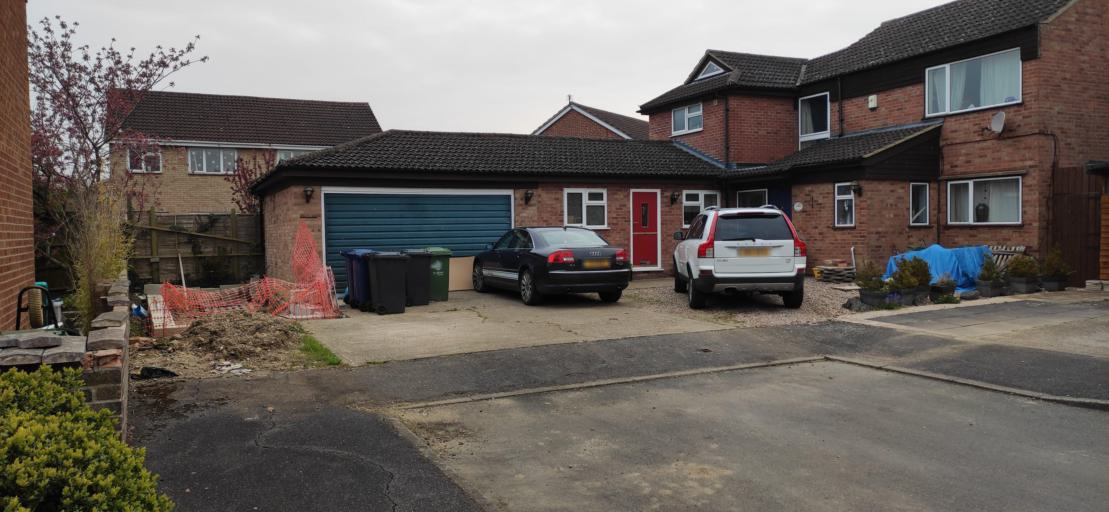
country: GB
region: England
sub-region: Cambridgeshire
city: Swavesey
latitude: 52.2505
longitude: 0.0121
